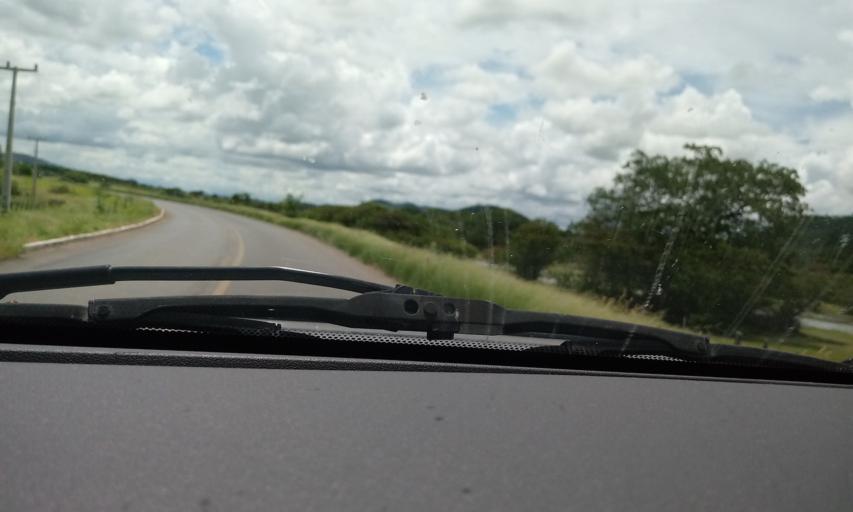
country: BR
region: Bahia
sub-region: Guanambi
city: Guanambi
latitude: -14.1830
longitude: -42.7980
